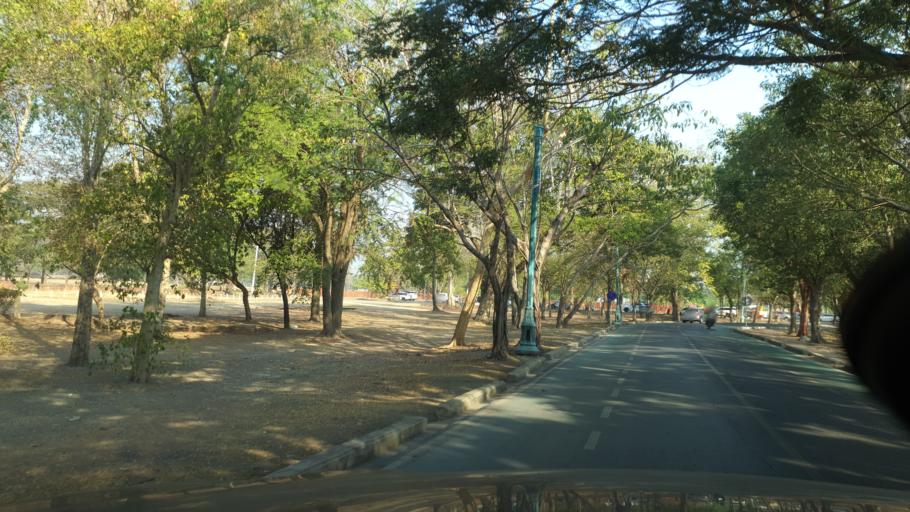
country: TH
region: Phra Nakhon Si Ayutthaya
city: Phra Nakhon Si Ayutthaya
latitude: 14.3561
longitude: 100.5616
